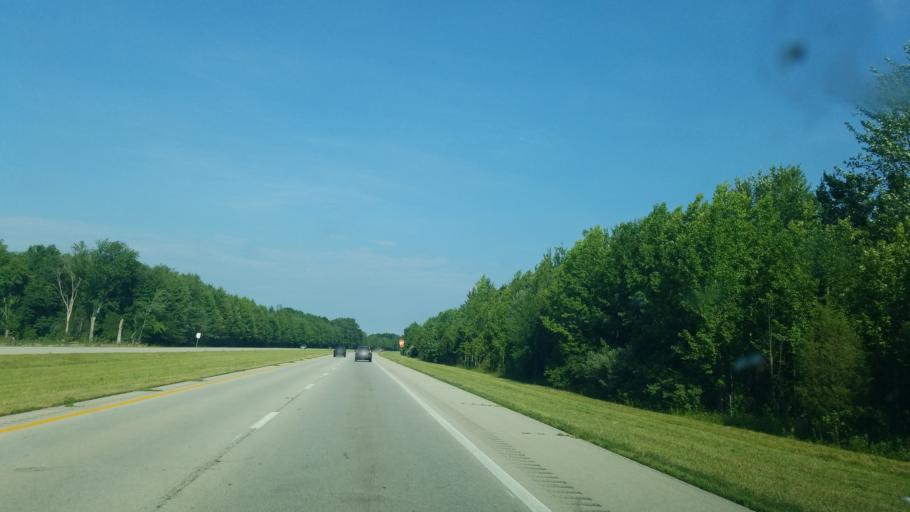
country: US
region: Ohio
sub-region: Clermont County
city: Williamsburg
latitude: 39.0601
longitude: -84.0035
